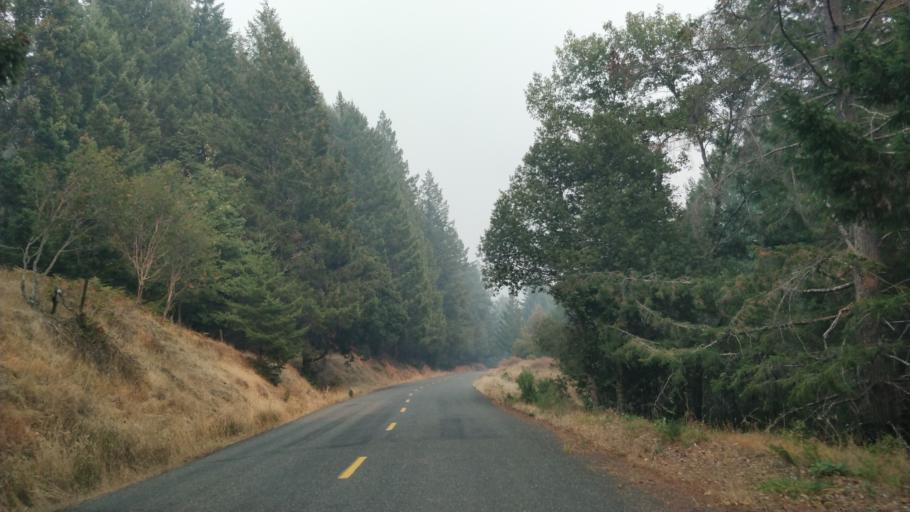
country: US
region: California
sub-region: Humboldt County
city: Rio Dell
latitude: 40.3292
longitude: -124.0381
